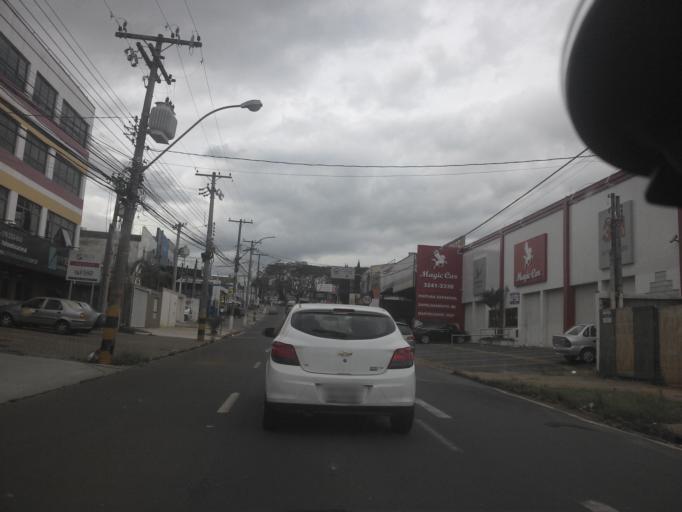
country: BR
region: Sao Paulo
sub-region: Campinas
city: Campinas
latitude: -22.8790
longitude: -47.0664
